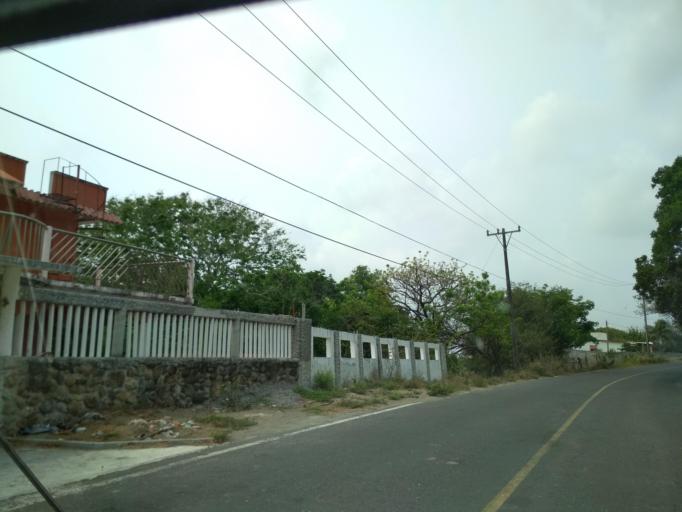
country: MX
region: Veracruz
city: Anton Lizardo
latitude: 19.0211
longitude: -95.9876
